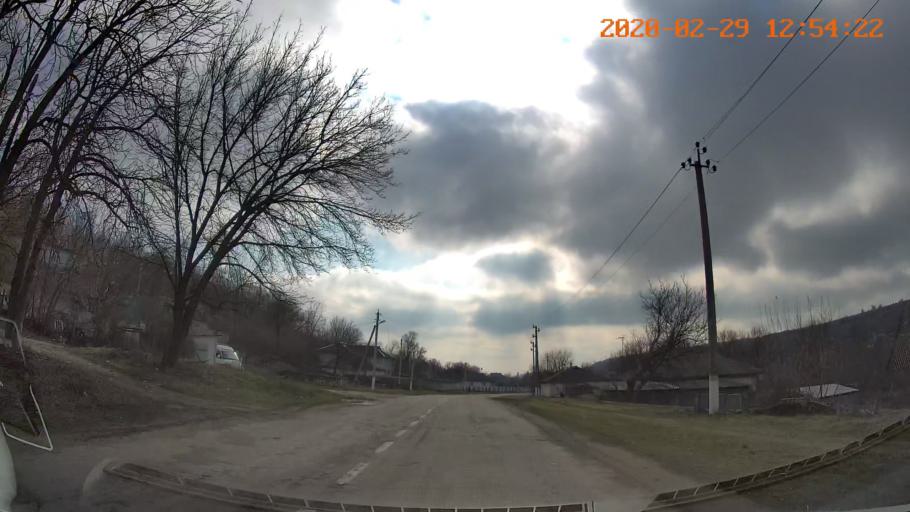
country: MD
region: Telenesti
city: Camenca
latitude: 48.1024
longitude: 28.7277
